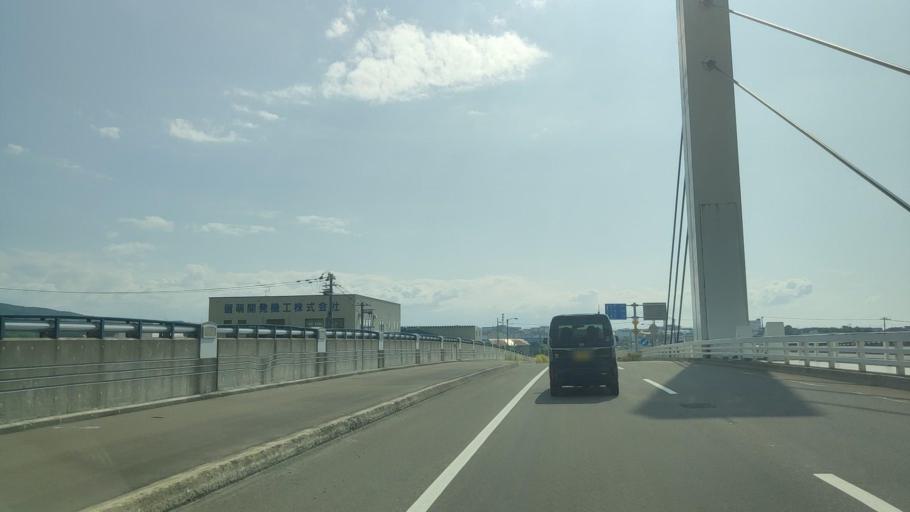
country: JP
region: Hokkaido
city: Rumoi
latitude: 43.9474
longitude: 141.6508
